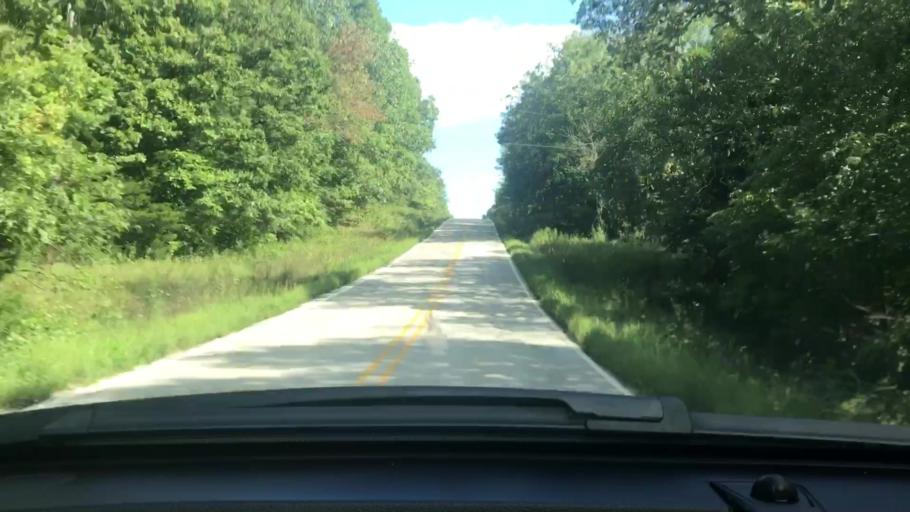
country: US
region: Missouri
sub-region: Wright County
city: Hartville
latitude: 37.3846
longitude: -92.4416
